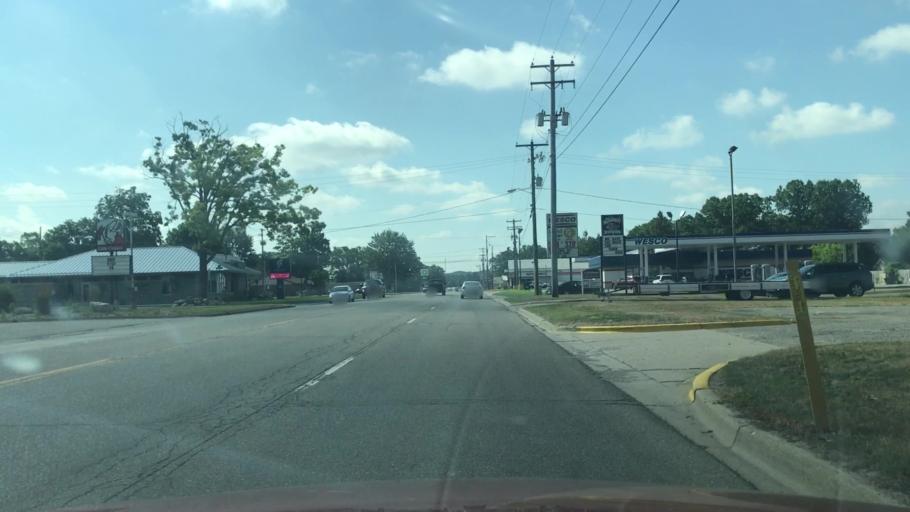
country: US
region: Michigan
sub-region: Newaygo County
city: Newaygo
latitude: 43.4116
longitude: -85.8069
